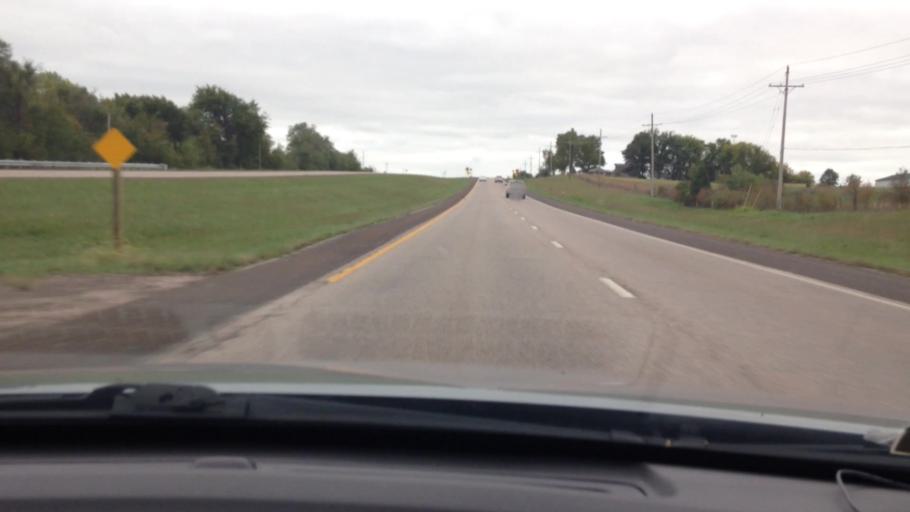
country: US
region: Kansas
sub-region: Leavenworth County
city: Lansing
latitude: 39.1976
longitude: -94.9005
